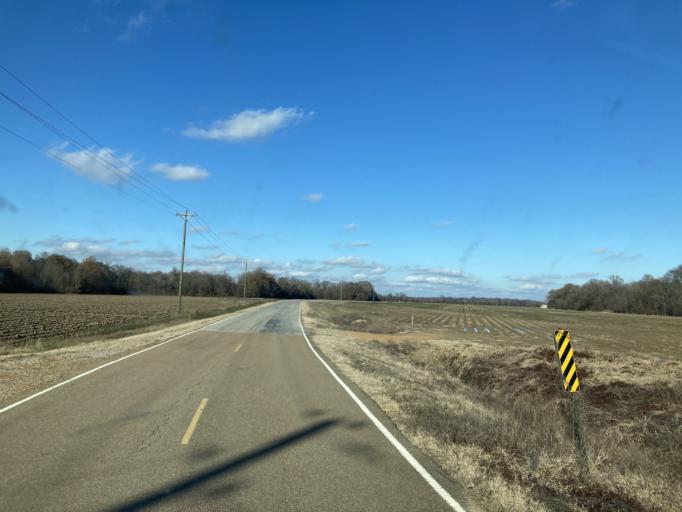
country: US
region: Mississippi
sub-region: Yazoo County
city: Yazoo City
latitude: 32.9485
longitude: -90.5081
